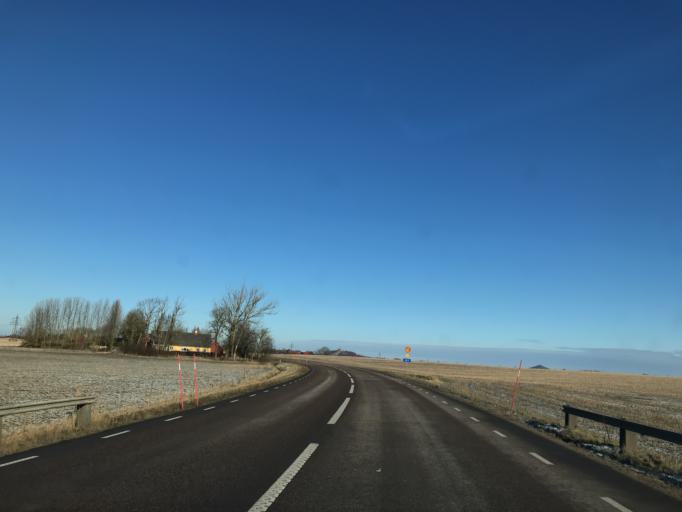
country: SE
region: Skane
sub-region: Bjuvs Kommun
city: Bjuv
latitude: 56.1054
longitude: 12.8960
